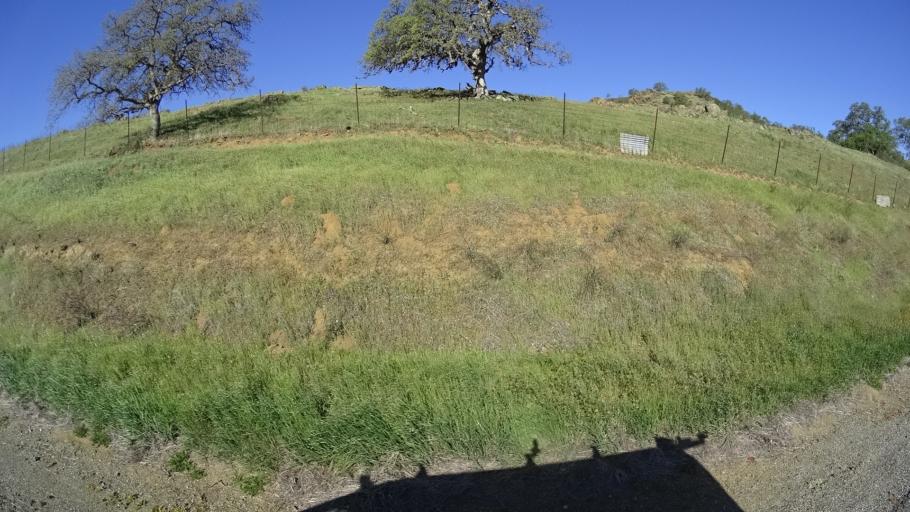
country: US
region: California
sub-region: Tehama County
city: Rancho Tehama Reserve
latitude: 39.7671
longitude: -122.5229
